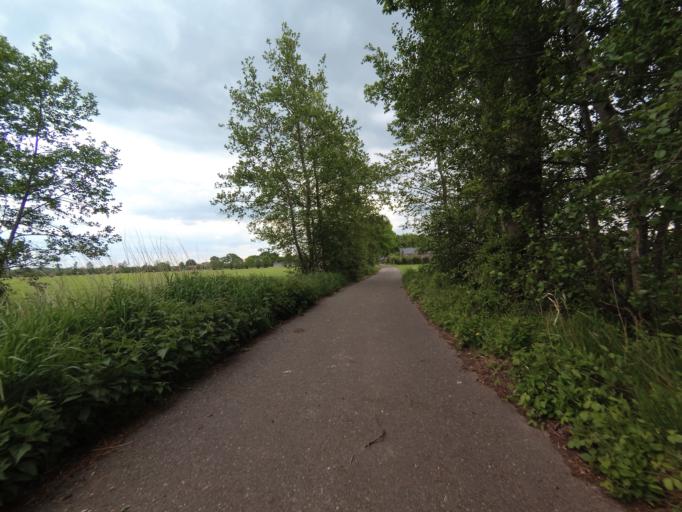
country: NL
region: Utrecht
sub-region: Gemeente Leusden
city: Leusden
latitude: 52.1588
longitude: 5.4382
